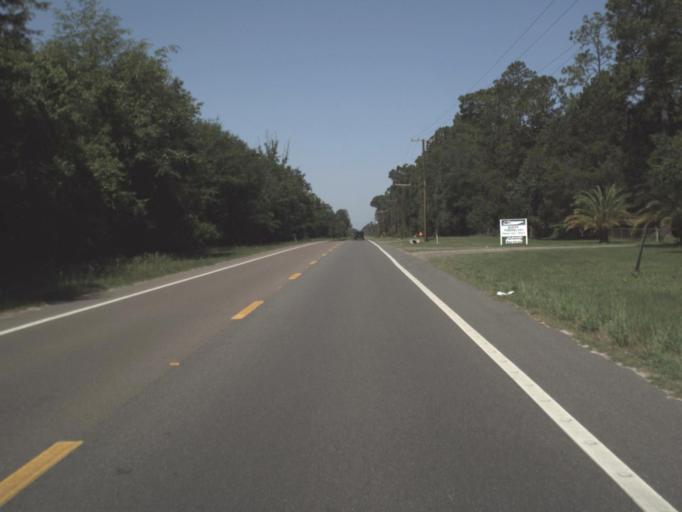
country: US
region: Florida
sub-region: Baker County
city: Macclenny
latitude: 30.2722
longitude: -82.1798
